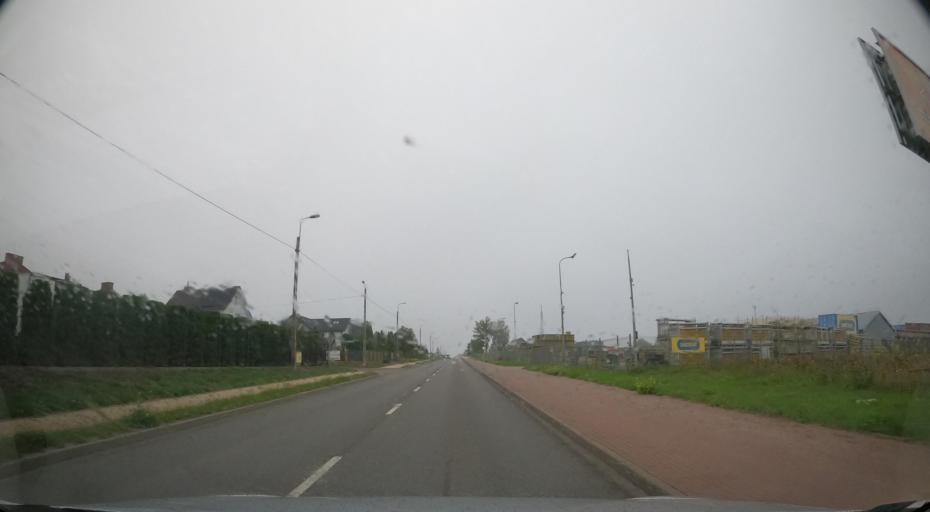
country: PL
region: Pomeranian Voivodeship
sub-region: Powiat kartuski
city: Chwaszczyno
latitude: 54.4431
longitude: 18.4068
